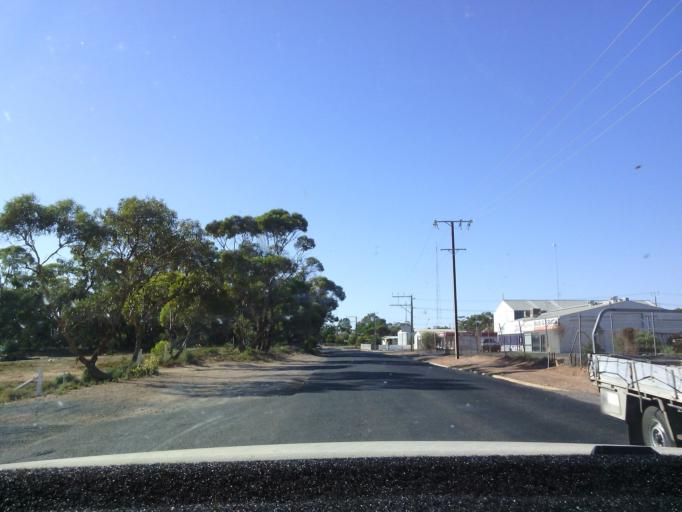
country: AU
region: South Australia
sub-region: Berri and Barmera
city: Berri
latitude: -34.2694
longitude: 140.6040
